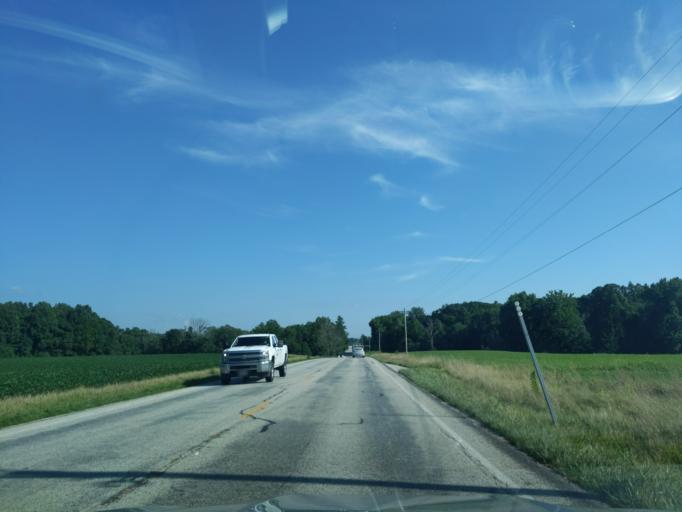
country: US
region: Indiana
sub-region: Ripley County
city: Versailles
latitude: 39.0888
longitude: -85.2754
